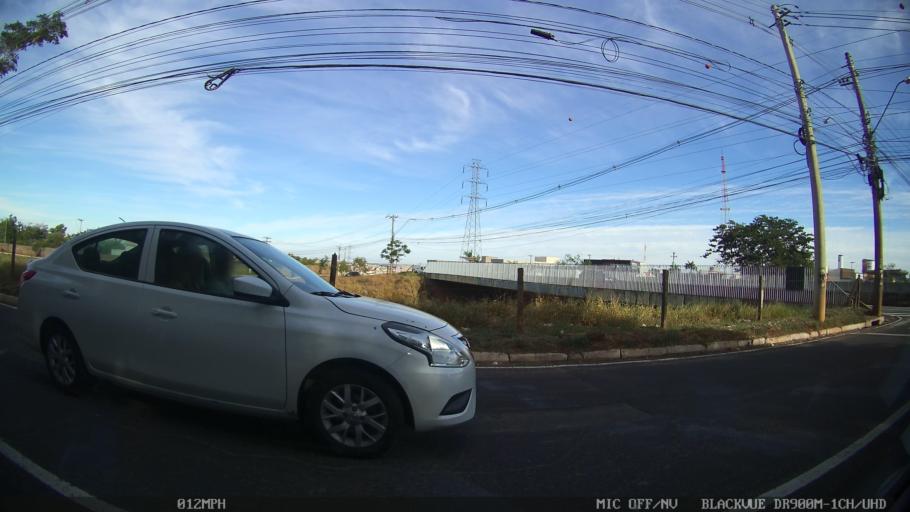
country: BR
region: Sao Paulo
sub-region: Sao Jose Do Rio Preto
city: Sao Jose do Rio Preto
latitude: -20.8010
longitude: -49.3453
